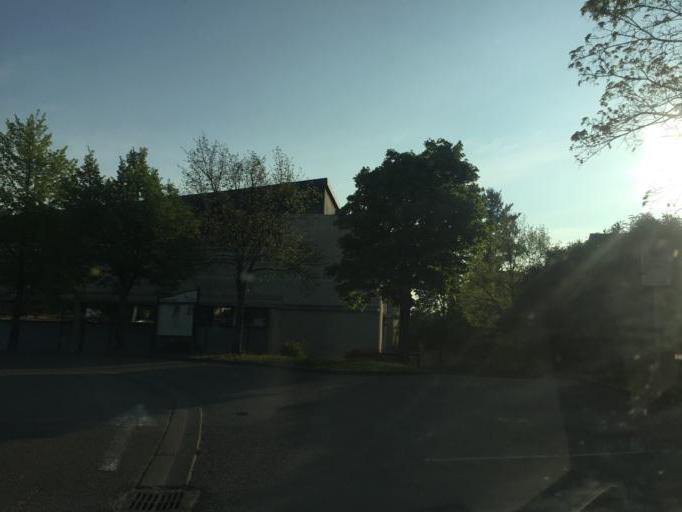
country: FR
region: Rhone-Alpes
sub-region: Departement de l'Ain
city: Miribel
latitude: 45.8267
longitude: 4.9571
